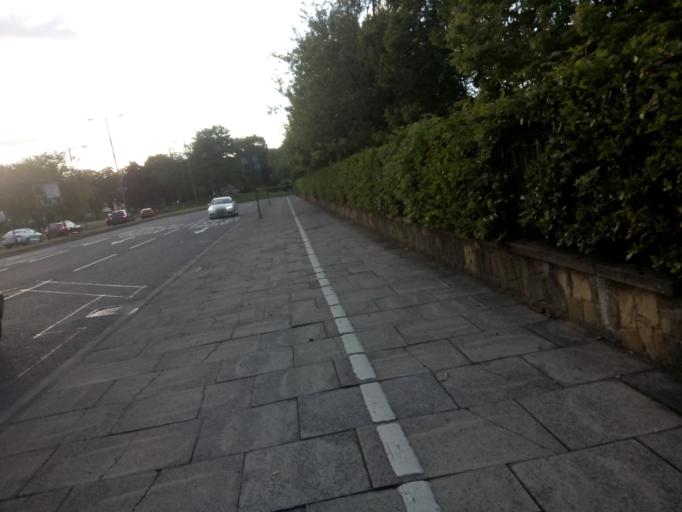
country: GB
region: England
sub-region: County Durham
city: Durham
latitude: 54.7841
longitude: -1.5855
